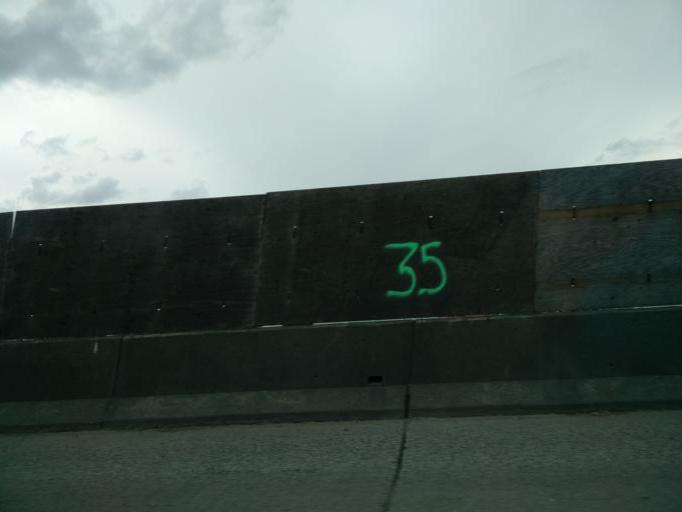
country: CA
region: British Columbia
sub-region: Fraser Valley Regional District
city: North Vancouver
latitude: 49.2976
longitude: -123.0265
